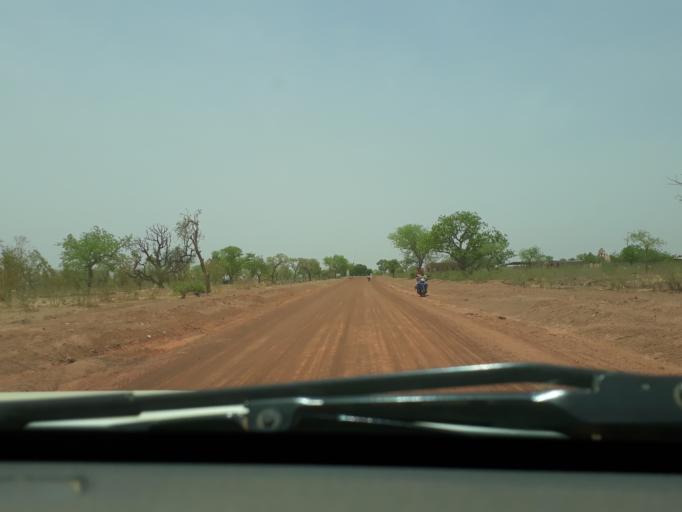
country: BF
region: Plateau-Central
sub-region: Province d'Oubritenga
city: Ziniare
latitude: 12.5794
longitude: -1.3335
